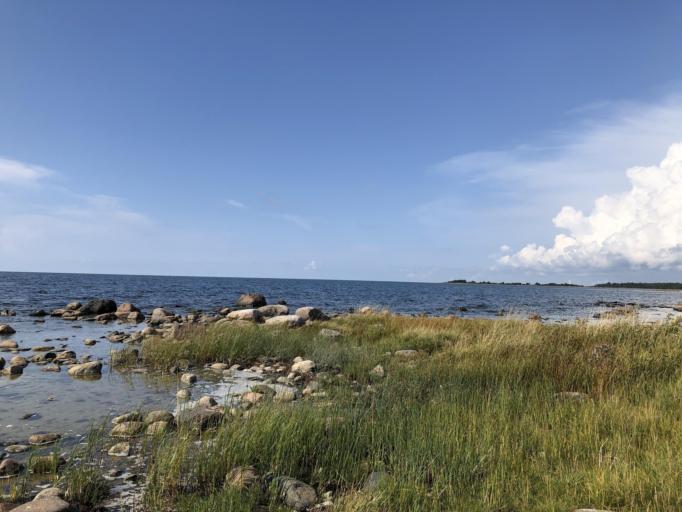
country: SE
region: Gotland
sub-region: Gotland
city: Hemse
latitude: 56.9953
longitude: 18.1938
